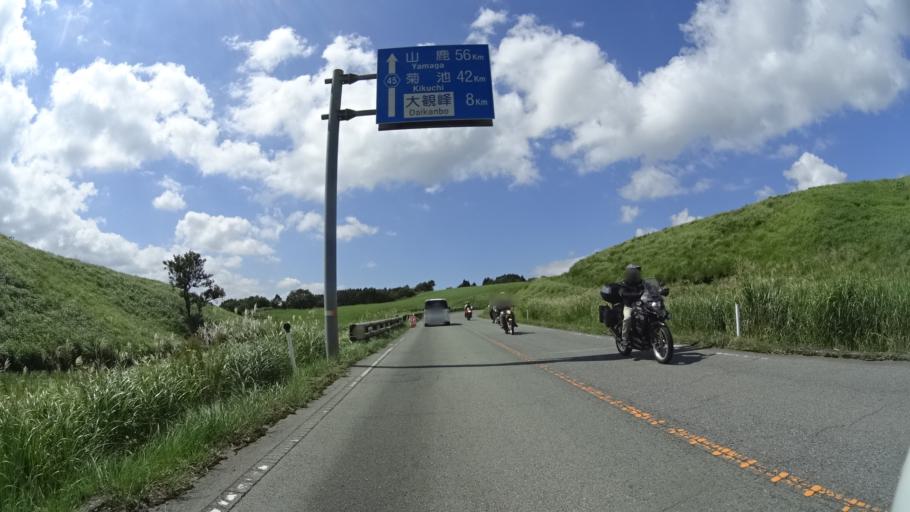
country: JP
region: Kumamoto
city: Aso
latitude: 33.0019
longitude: 131.1367
